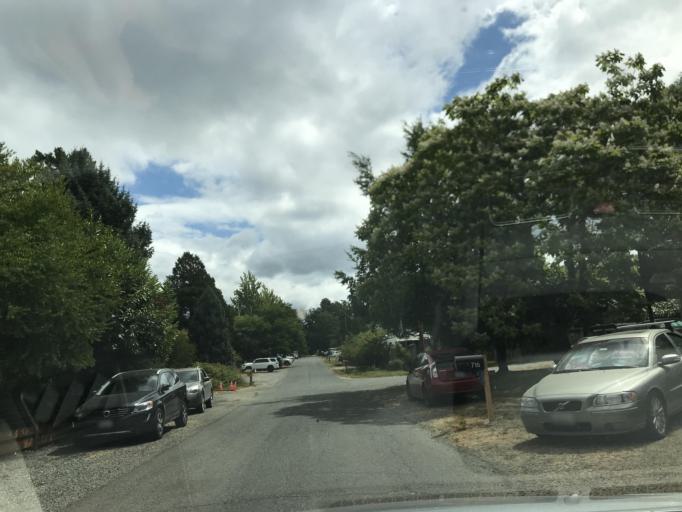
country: US
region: Washington
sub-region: Whatcom County
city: Bellingham
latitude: 48.7177
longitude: -122.5074
